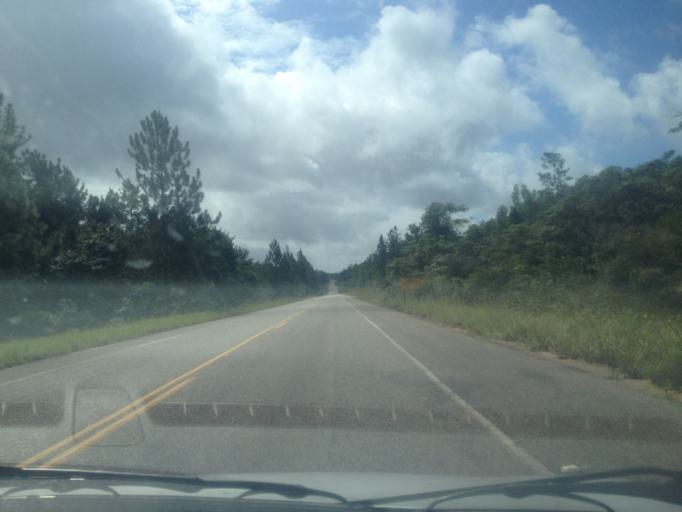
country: BR
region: Bahia
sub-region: Entre Rios
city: Entre Rios
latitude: -12.1505
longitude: -37.7995
